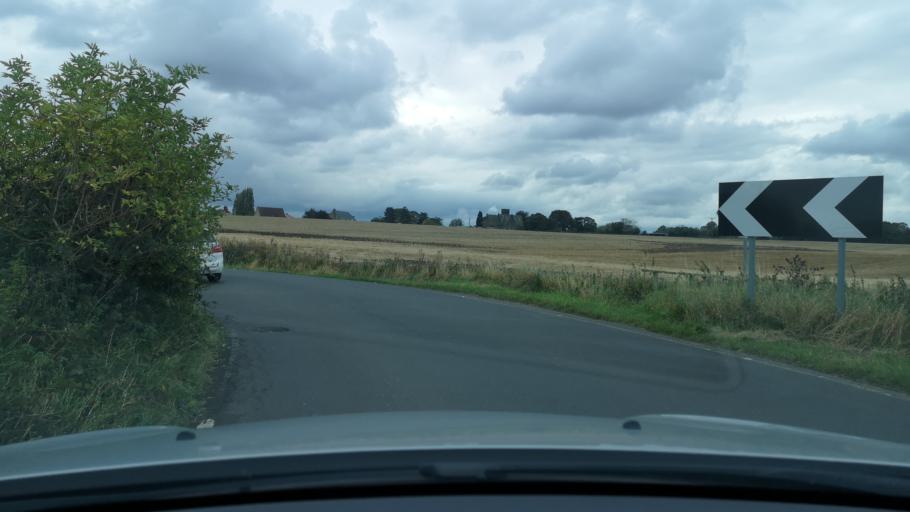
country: GB
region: England
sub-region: City and Borough of Wakefield
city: Darrington
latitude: 53.6651
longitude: -1.2965
